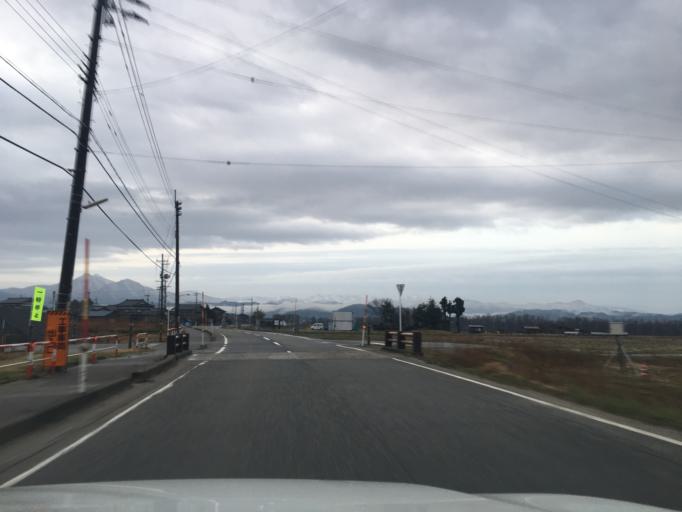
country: JP
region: Niigata
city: Murakami
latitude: 38.2765
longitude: 139.5227
